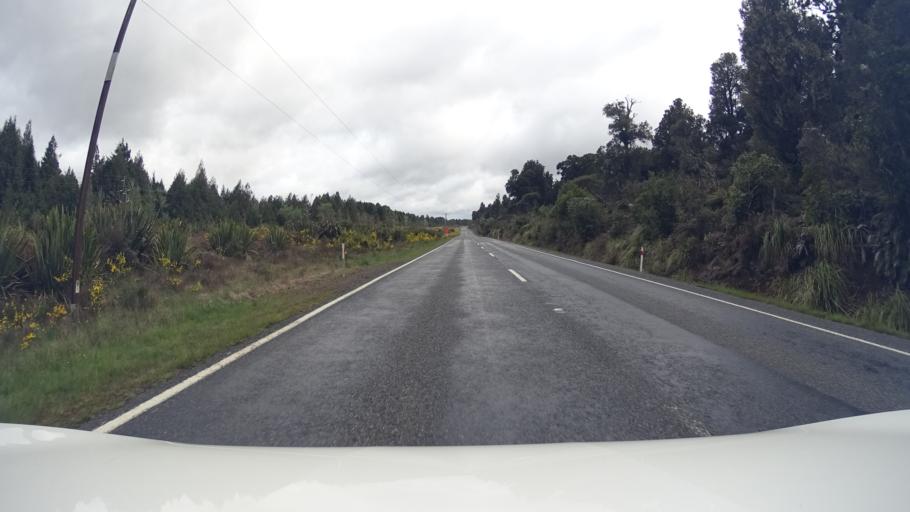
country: NZ
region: Manawatu-Wanganui
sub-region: Ruapehu District
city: Waiouru
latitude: -39.2541
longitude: 175.3879
